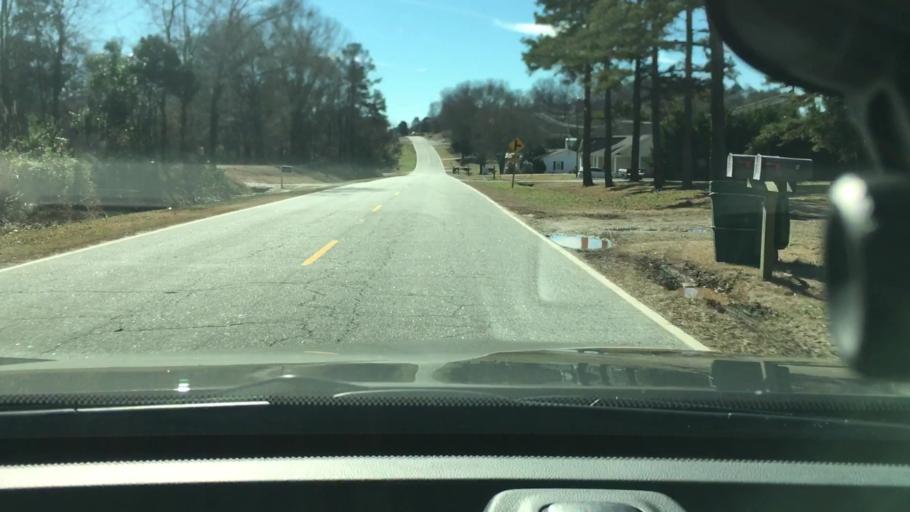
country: US
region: South Carolina
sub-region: Cherokee County
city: Gaffney
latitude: 35.0425
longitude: -81.6765
